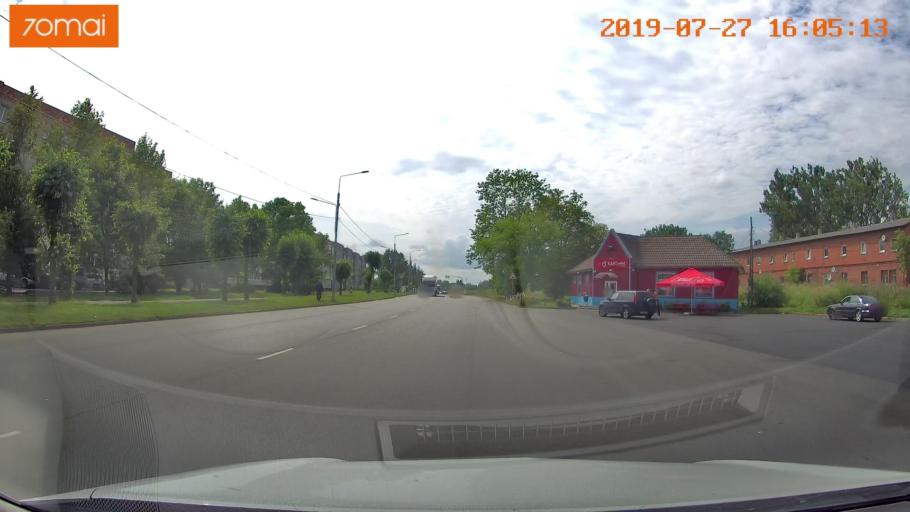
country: RU
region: Kaliningrad
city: Chernyakhovsk
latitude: 54.6352
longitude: 21.7924
